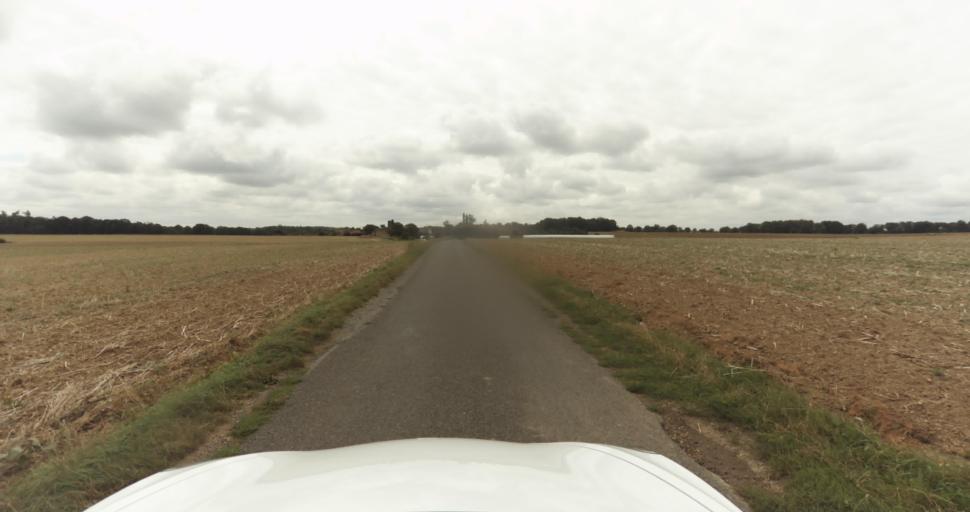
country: FR
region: Haute-Normandie
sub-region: Departement de l'Eure
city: Saint-Sebastien-de-Morsent
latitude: 49.0222
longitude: 1.0606
